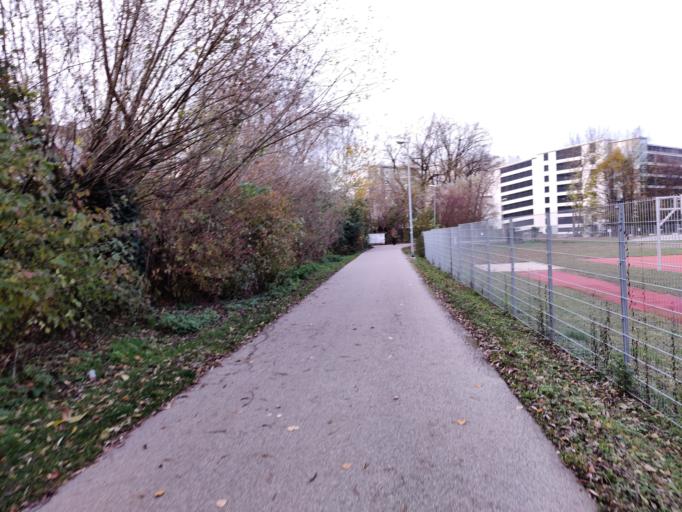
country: AT
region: Lower Austria
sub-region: Sankt Polten Stadt
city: Sankt Poelten
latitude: 48.2112
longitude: 15.6300
